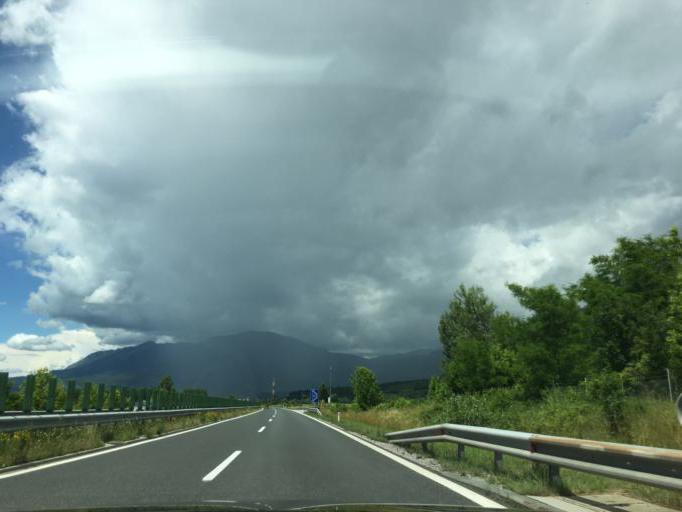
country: SI
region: Vipava
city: Vipava
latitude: 45.8640
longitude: 13.9356
